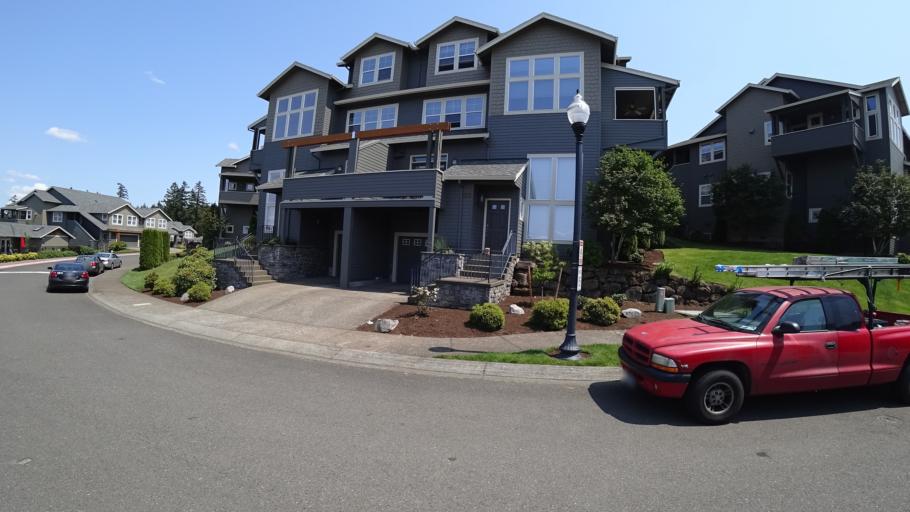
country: US
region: Oregon
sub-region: Multnomah County
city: Lents
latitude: 45.4594
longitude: -122.5579
